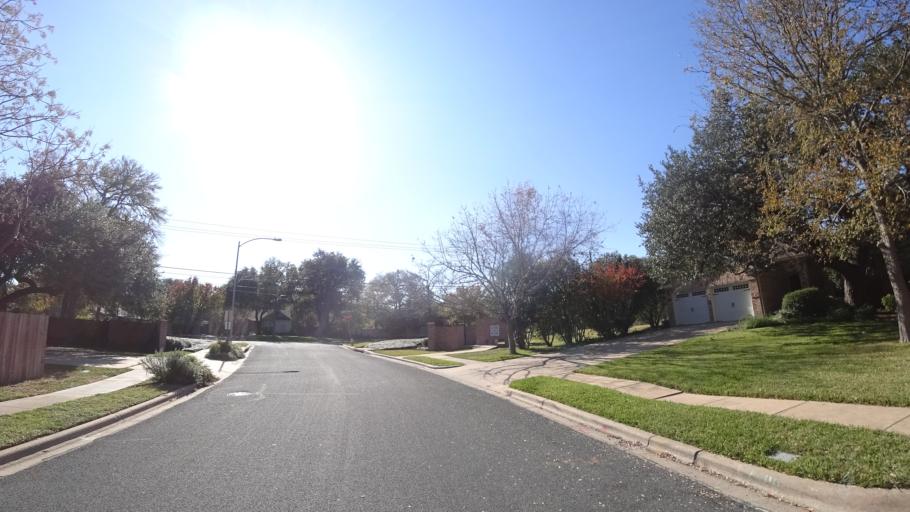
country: US
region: Texas
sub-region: Travis County
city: Shady Hollow
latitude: 30.2239
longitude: -97.8638
